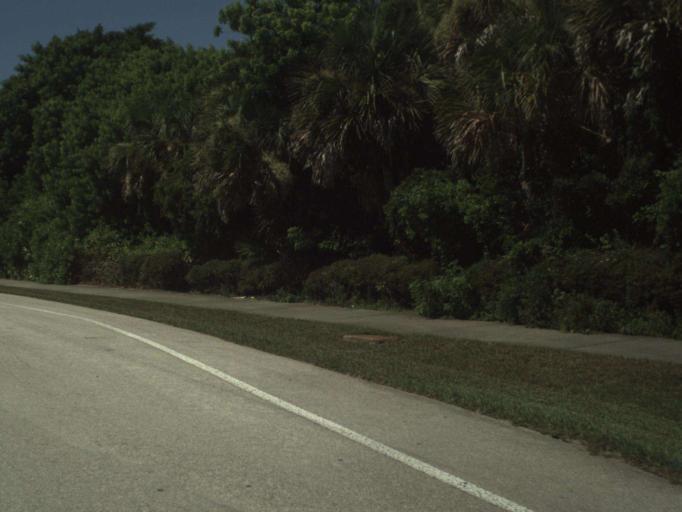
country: US
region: Florida
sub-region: Indian River County
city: Wabasso Beach
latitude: 27.7618
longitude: -80.3978
